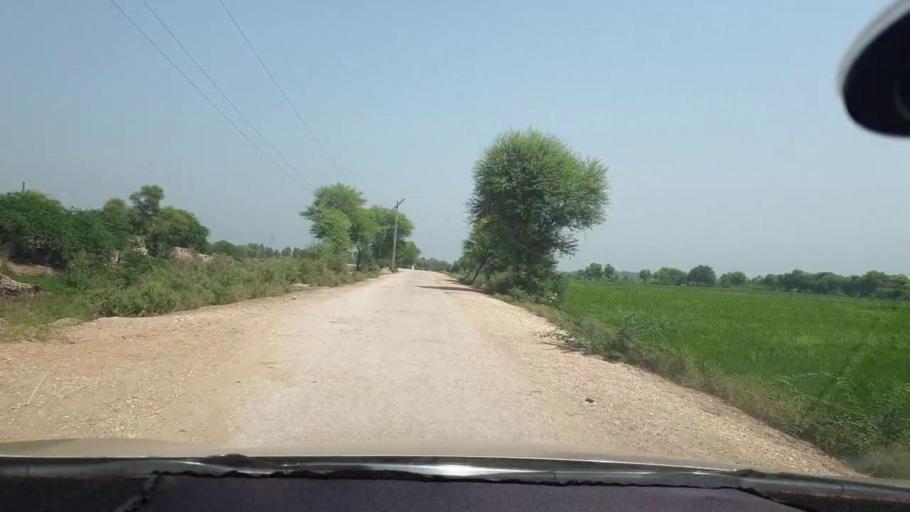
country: PK
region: Sindh
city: Kambar
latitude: 27.6602
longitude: 67.8810
